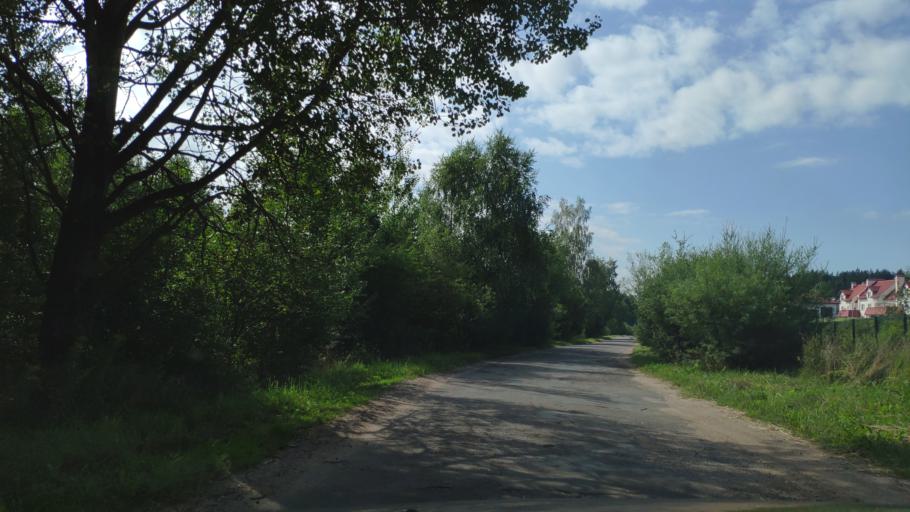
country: BY
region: Minsk
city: Zaslawye
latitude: 53.9862
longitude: 27.2888
